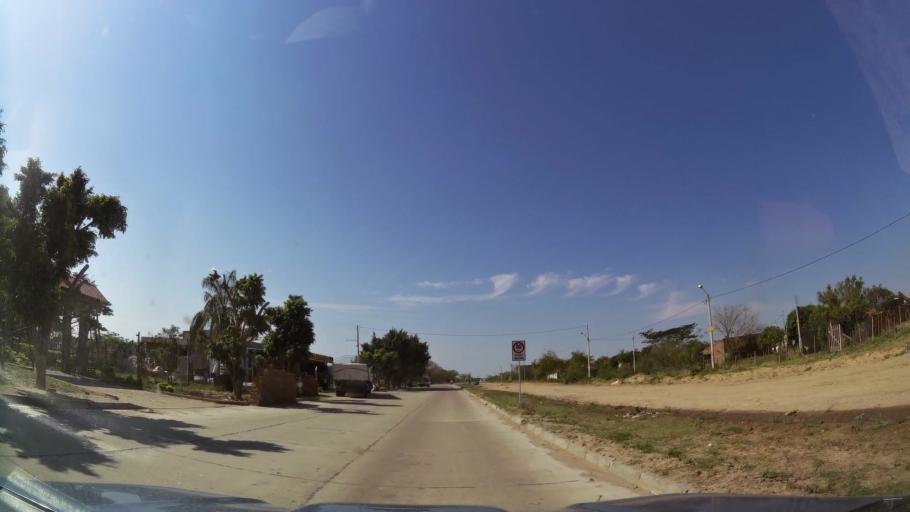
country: BO
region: Santa Cruz
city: Cotoca
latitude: -17.7198
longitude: -63.0746
